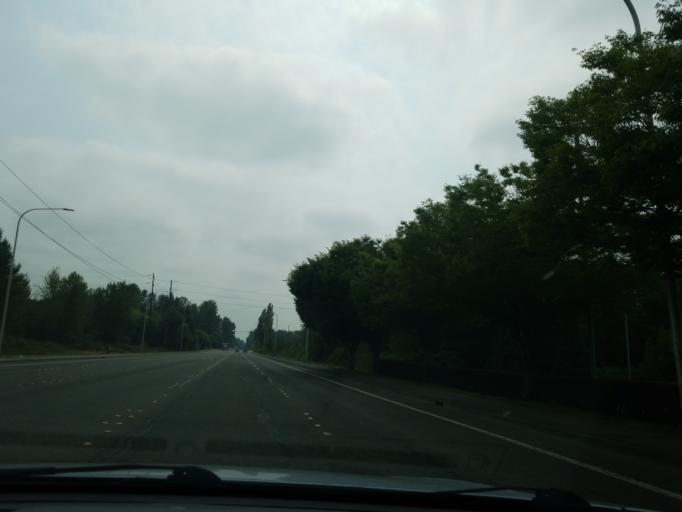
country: US
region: Washington
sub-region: King County
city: Renton
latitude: 47.4603
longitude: -122.2330
